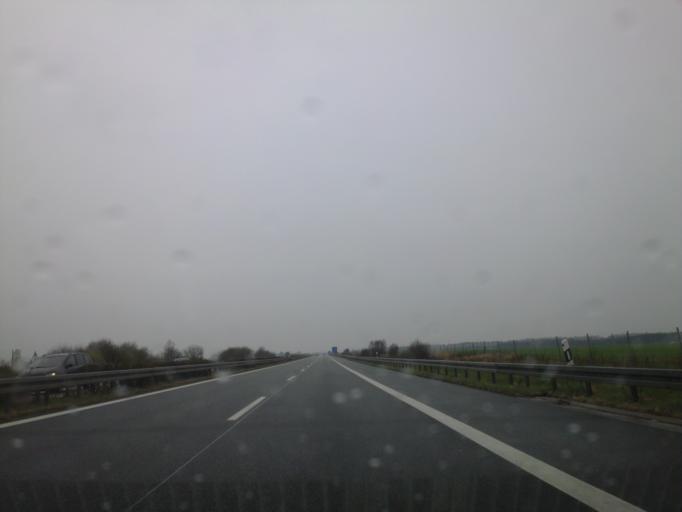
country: DE
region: Mecklenburg-Vorpommern
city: Dummerstorf
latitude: 54.0258
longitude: 12.2619
